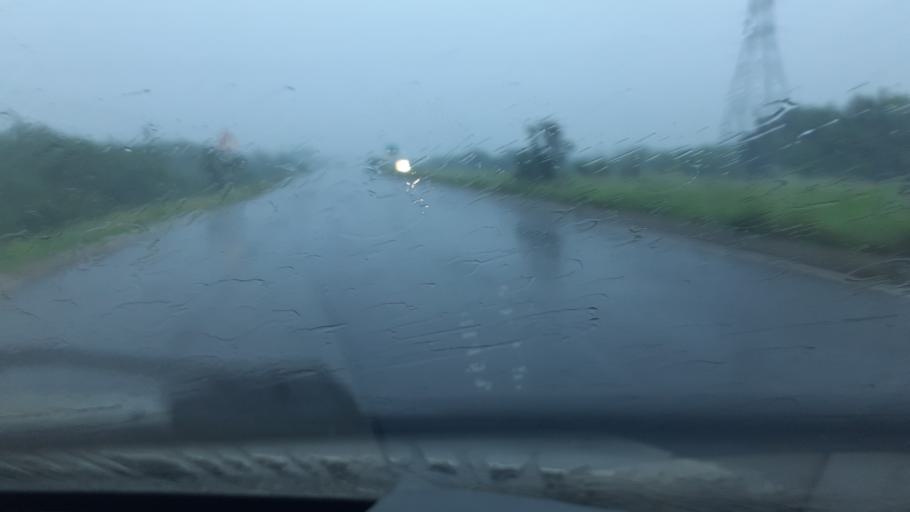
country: IN
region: Tamil Nadu
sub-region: Virudhunagar
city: Virudunagar
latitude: 9.5045
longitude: 77.9418
